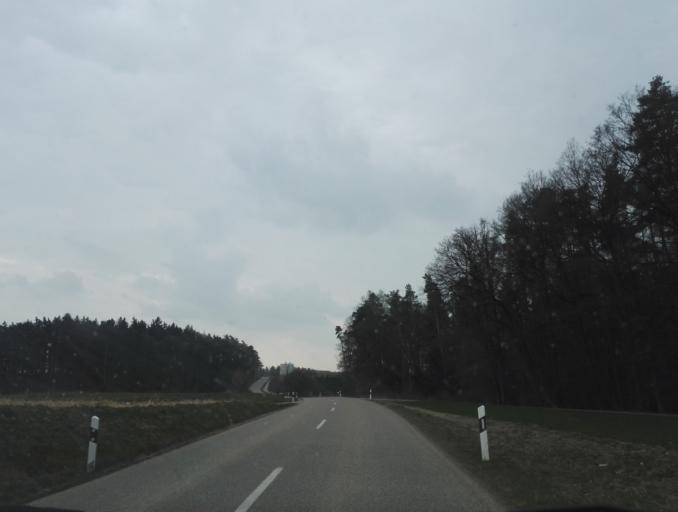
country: DE
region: Bavaria
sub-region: Lower Bavaria
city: Rottenburg an der Laaber
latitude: 48.6756
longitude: 12.0260
